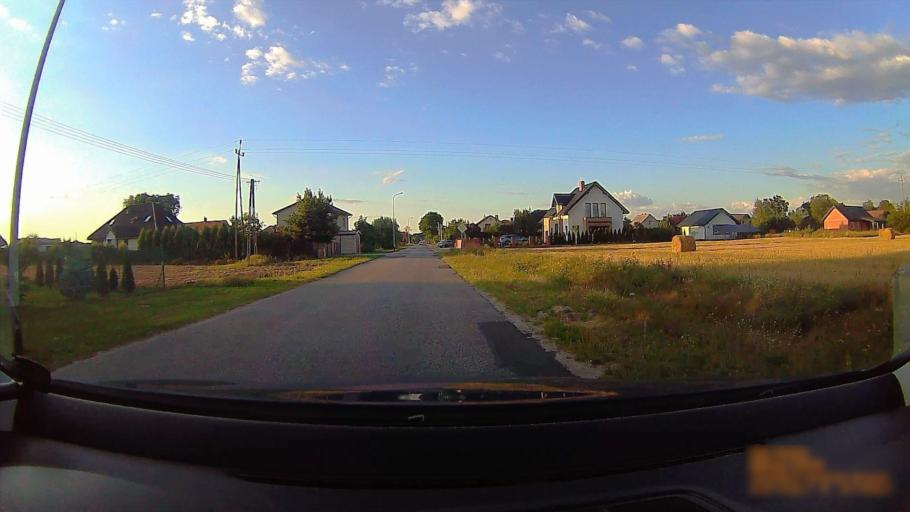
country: PL
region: Greater Poland Voivodeship
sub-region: Konin
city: Konin
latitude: 52.2083
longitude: 18.3239
